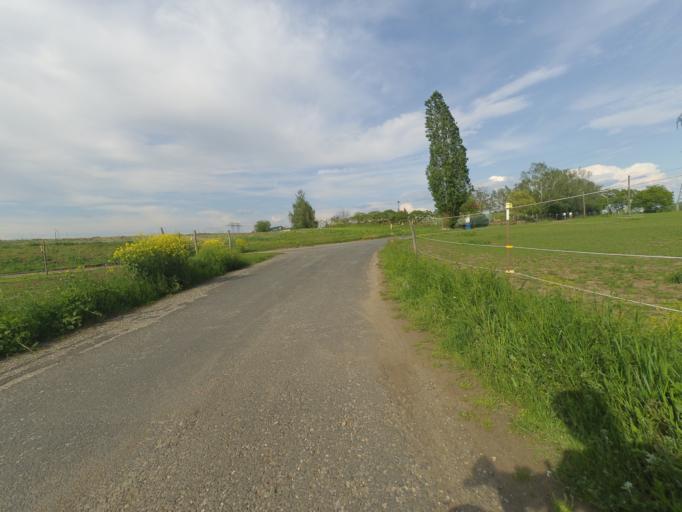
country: DE
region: Saxony
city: Coswig
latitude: 51.0993
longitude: 13.6042
